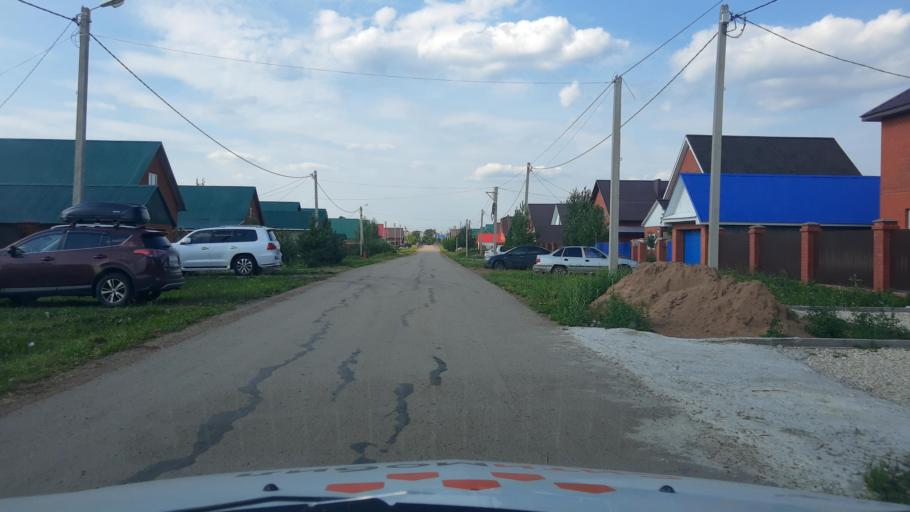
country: RU
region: Bashkortostan
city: Kabakovo
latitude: 54.6615
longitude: 56.2123
